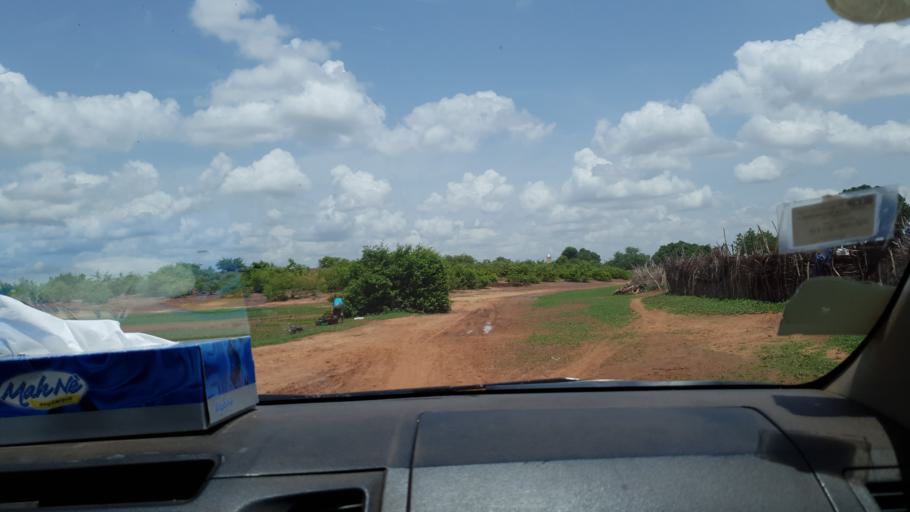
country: ML
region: Koulikoro
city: Banamba
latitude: 13.3757
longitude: -7.2202
